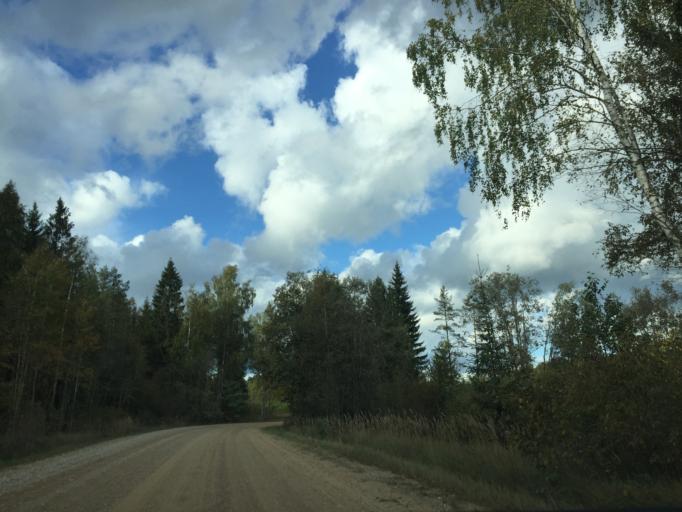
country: LV
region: Malpils
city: Malpils
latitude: 57.0241
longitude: 25.0507
